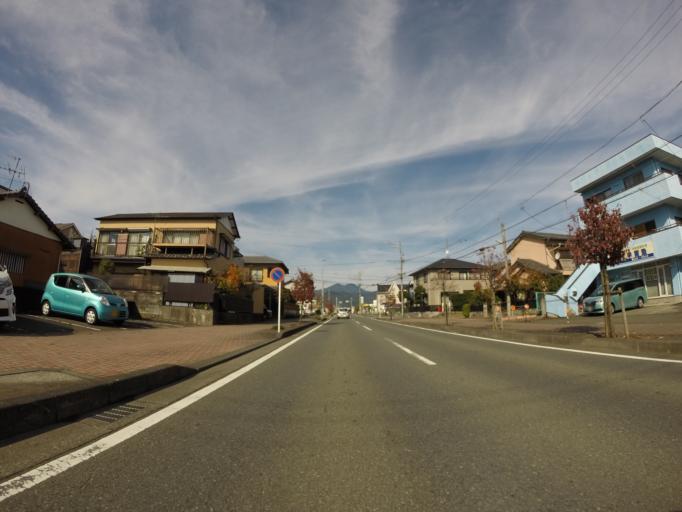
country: JP
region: Shizuoka
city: Shizuoka-shi
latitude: 35.0140
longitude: 138.4664
